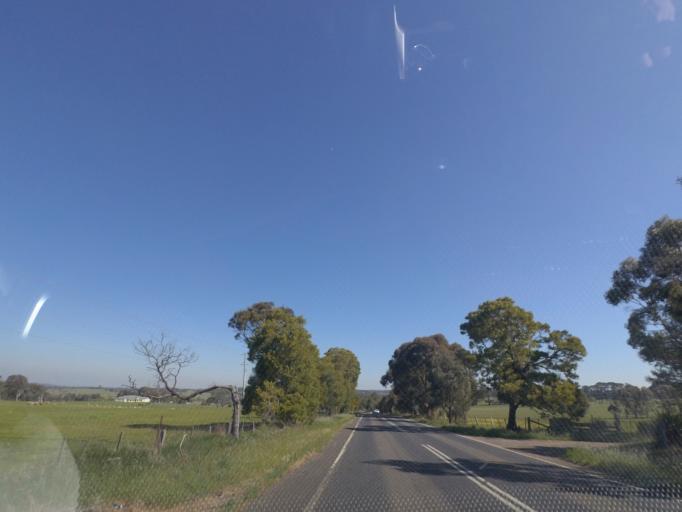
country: AU
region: Victoria
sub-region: Whittlesea
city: Whittlesea
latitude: -37.3335
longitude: 144.9832
